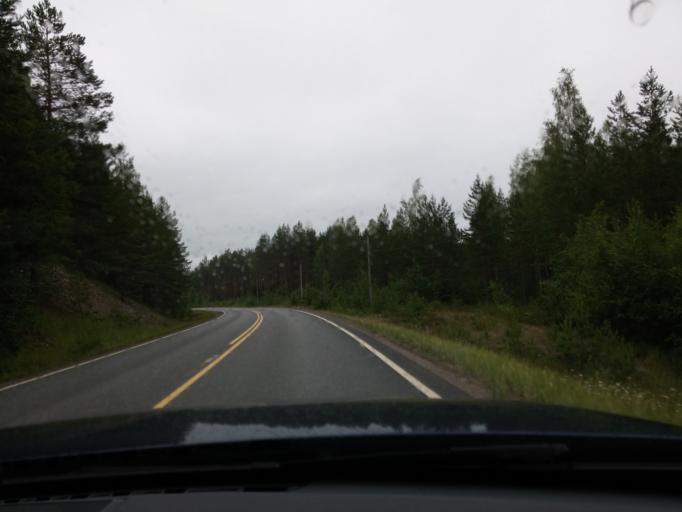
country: FI
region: Central Finland
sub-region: Joutsa
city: Joutsa
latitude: 61.7890
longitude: 26.0213
